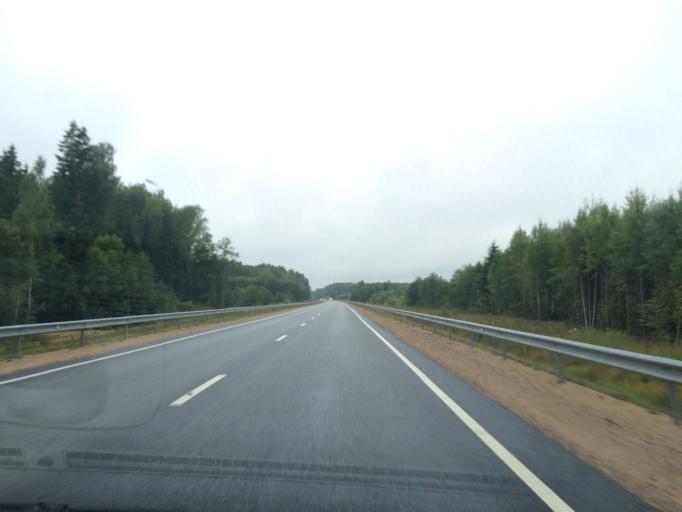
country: LV
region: Ogre
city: Jumprava
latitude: 56.7974
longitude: 24.9584
